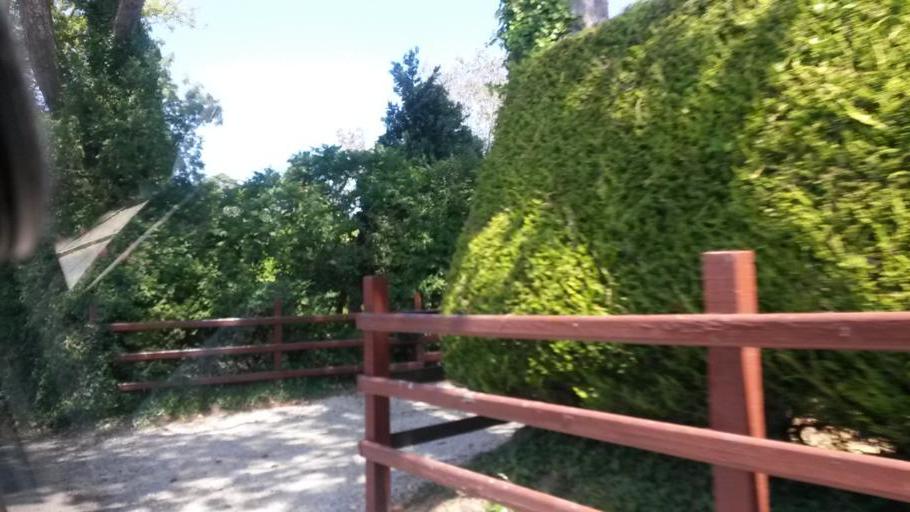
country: IE
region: Leinster
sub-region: An Mhi
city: Ashbourne
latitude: 53.5231
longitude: -6.3151
